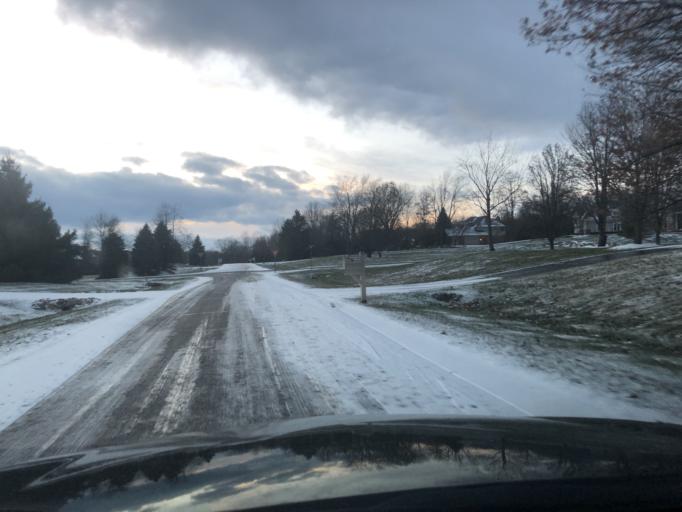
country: US
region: Michigan
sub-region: Oakland County
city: Milford
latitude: 42.5804
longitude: -83.6476
